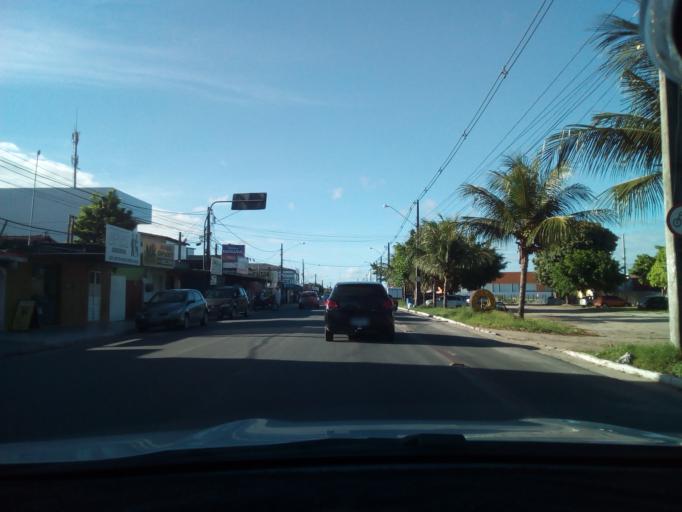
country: BR
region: Paraiba
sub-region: Joao Pessoa
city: Joao Pessoa
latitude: -7.1750
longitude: -34.8368
